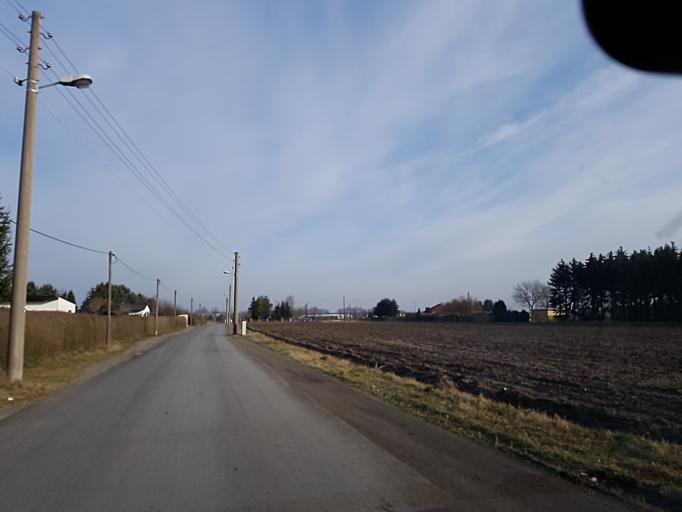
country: DE
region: Brandenburg
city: Finsterwalde
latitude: 51.6203
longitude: 13.7263
